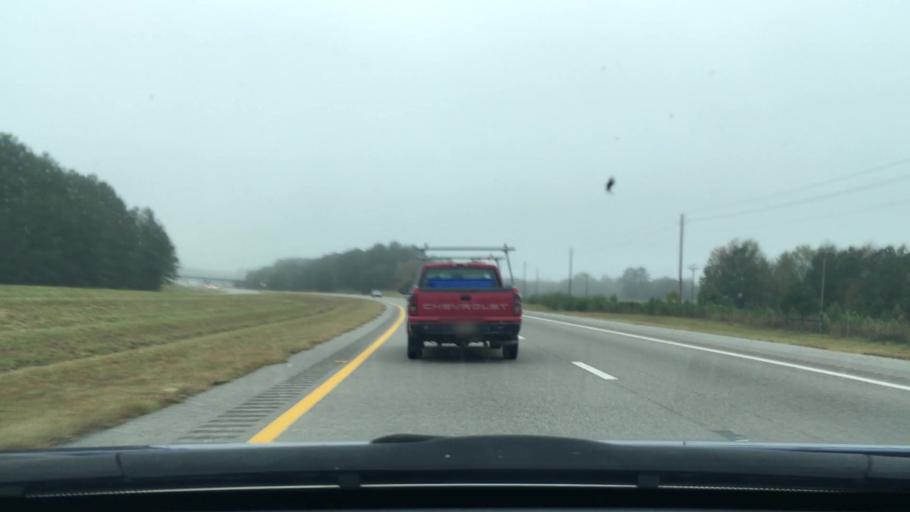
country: US
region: South Carolina
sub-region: Kershaw County
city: Camden
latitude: 34.2171
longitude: -80.5443
